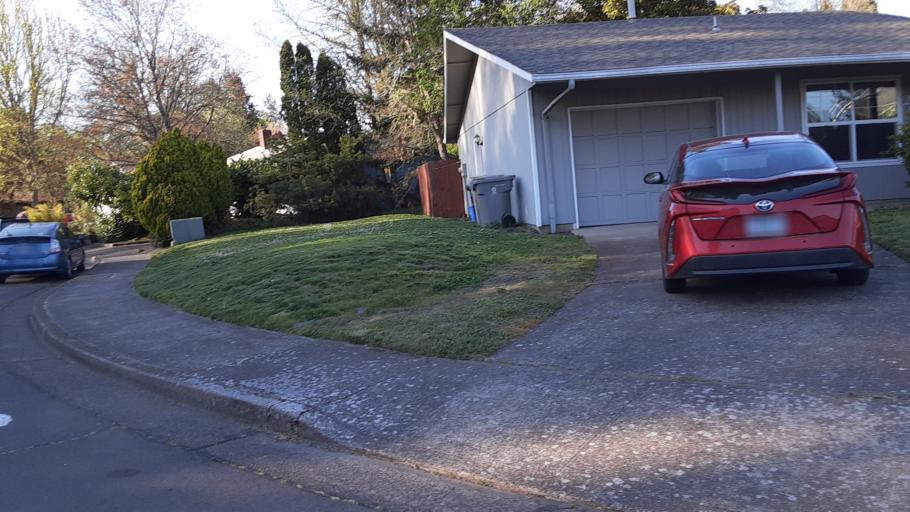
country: US
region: Oregon
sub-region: Benton County
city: Corvallis
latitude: 44.5463
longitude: -123.2562
